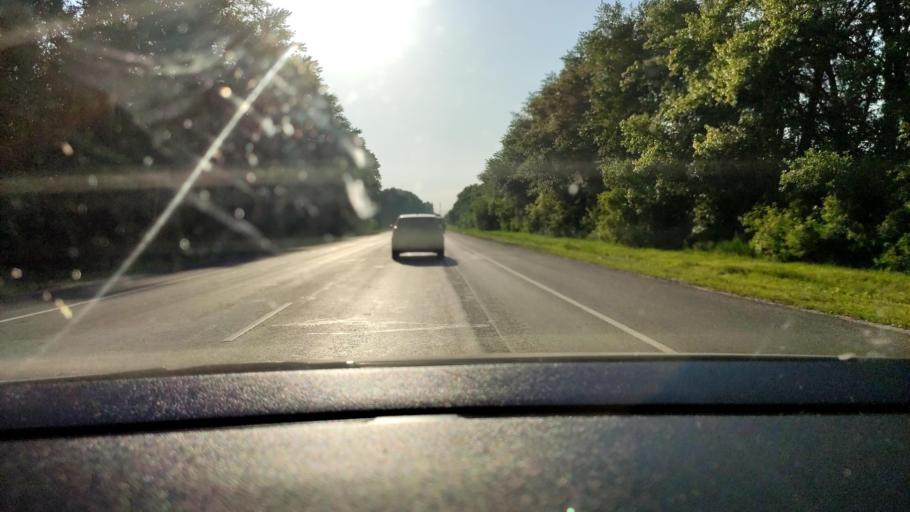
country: RU
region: Voronezj
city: Kashirskoye
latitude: 51.4954
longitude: 39.5982
